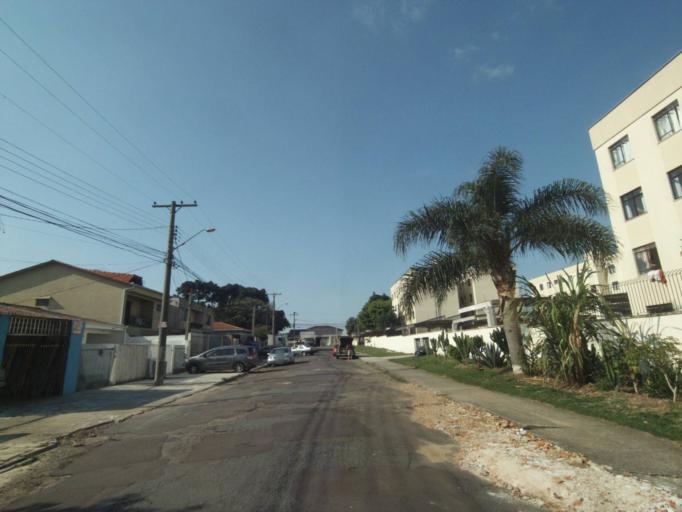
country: BR
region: Parana
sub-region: Curitiba
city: Curitiba
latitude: -25.4884
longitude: -49.3258
